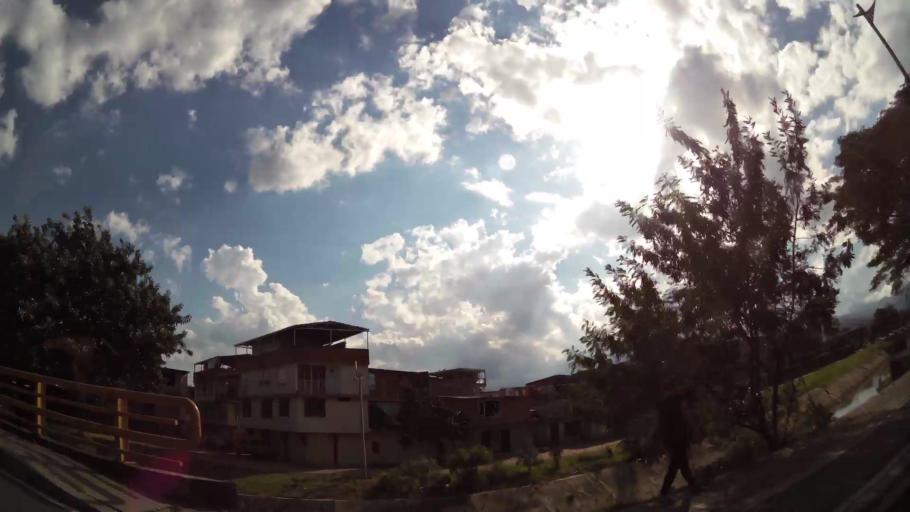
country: CO
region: Valle del Cauca
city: Cali
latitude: 3.4275
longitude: -76.4973
